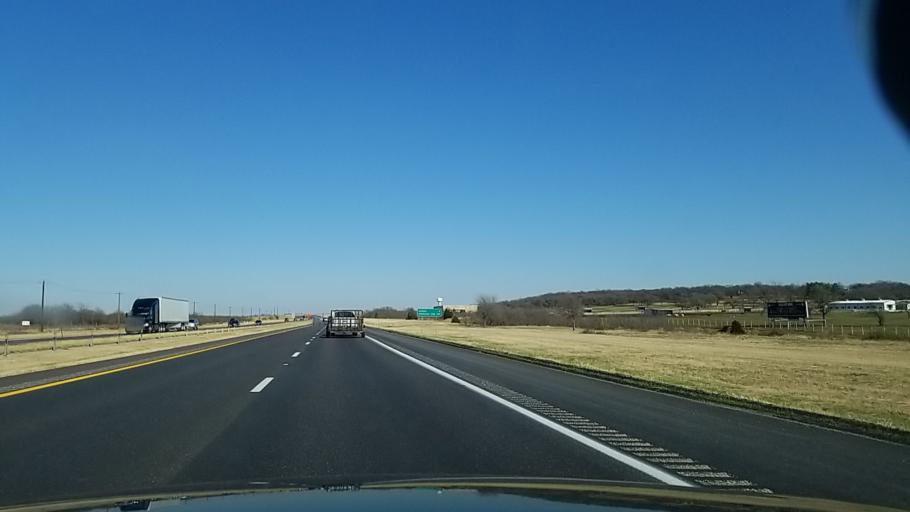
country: US
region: Texas
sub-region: Denton County
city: Argyle
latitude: 33.1105
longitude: -97.2187
